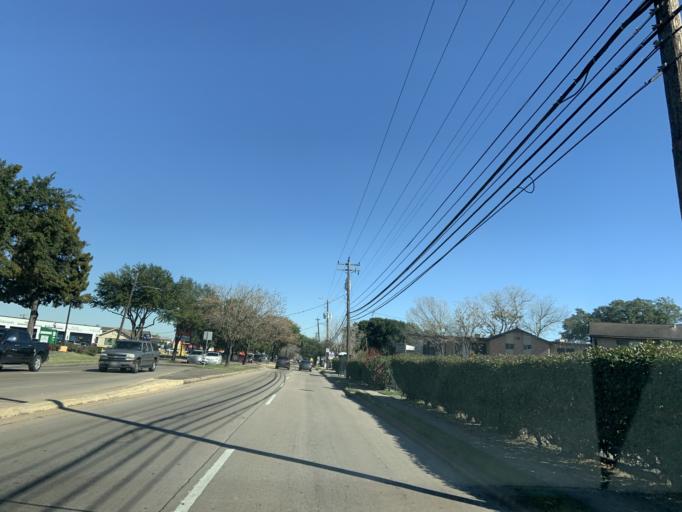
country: US
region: Texas
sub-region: Harris County
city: Bellaire
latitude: 29.6875
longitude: -95.5073
